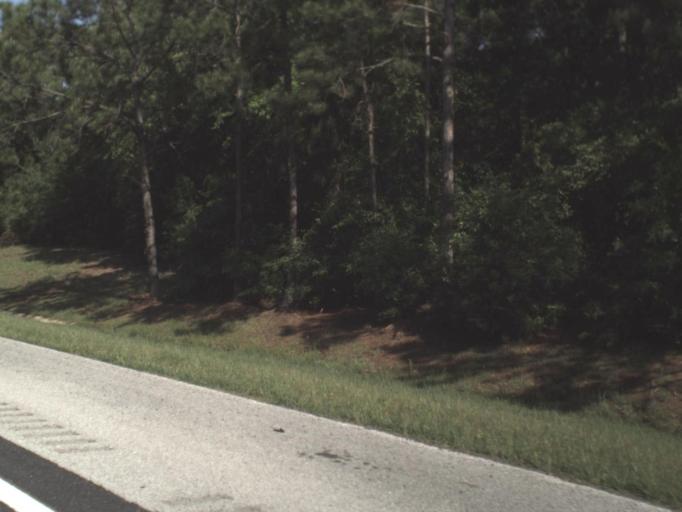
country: US
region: Florida
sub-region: Holmes County
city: Bonifay
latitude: 30.7636
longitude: -85.7104
